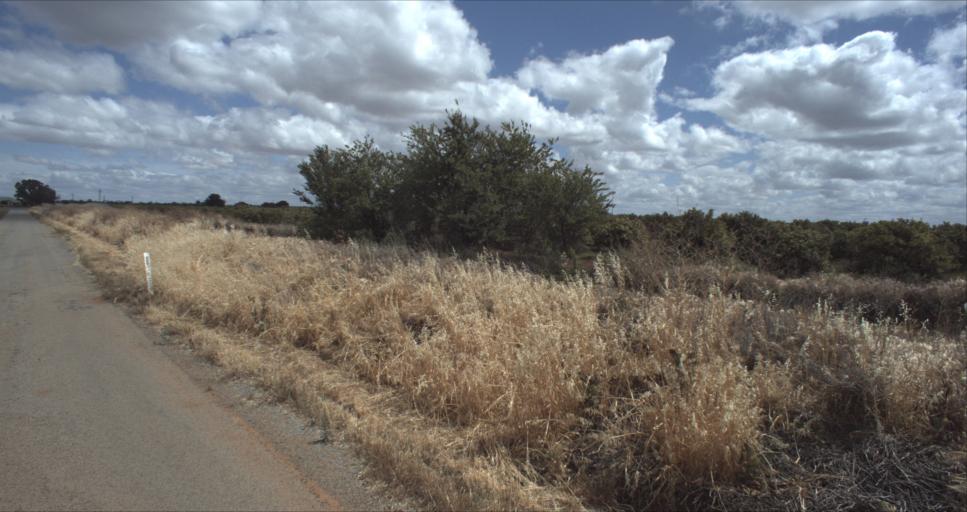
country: AU
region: New South Wales
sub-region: Leeton
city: Leeton
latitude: -34.5866
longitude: 146.3912
